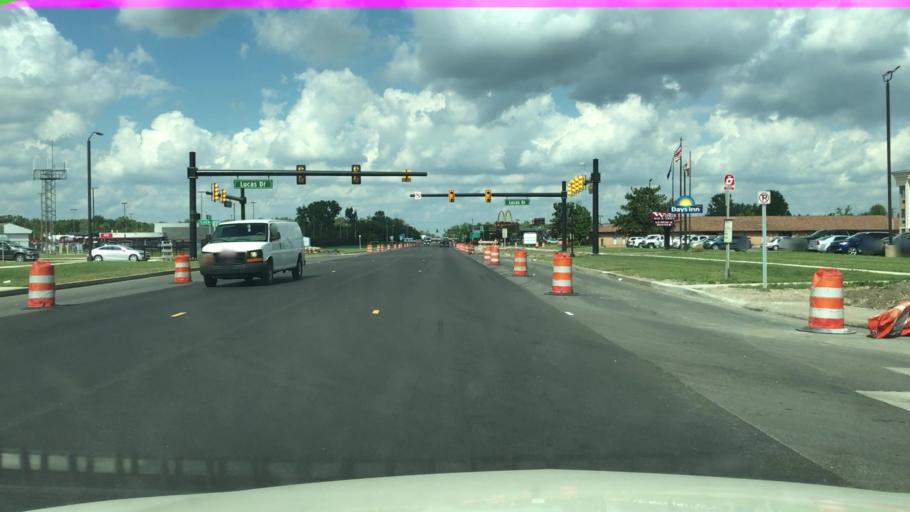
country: US
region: Michigan
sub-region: Wayne County
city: Taylor
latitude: 42.2353
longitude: -83.3277
